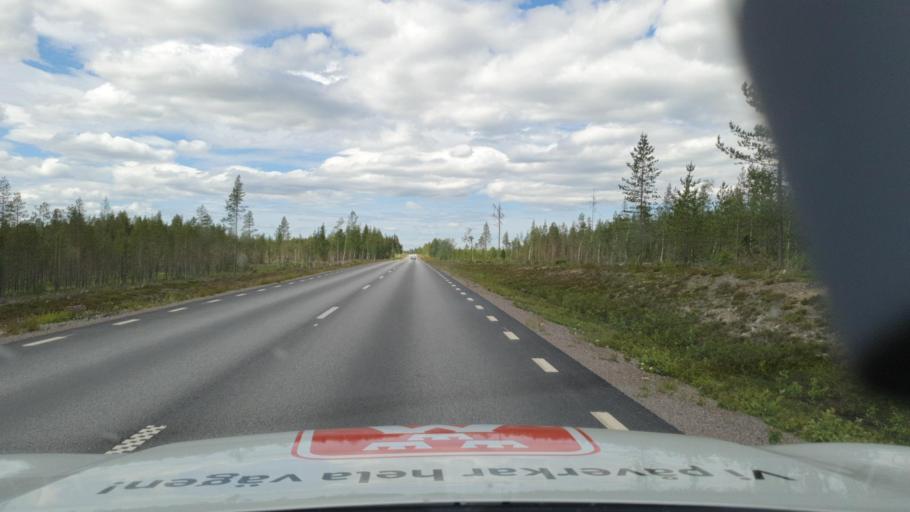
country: SE
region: Vaesterbotten
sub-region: Skelleftea Kommun
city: Langsele
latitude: 65.1167
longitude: 19.9570
